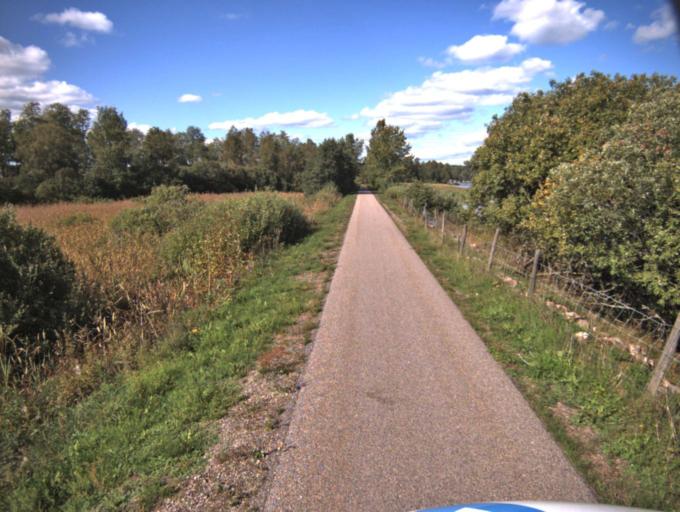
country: SE
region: Vaestra Goetaland
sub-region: Ulricehamns Kommun
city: Ulricehamn
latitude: 57.8415
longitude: 13.3030
